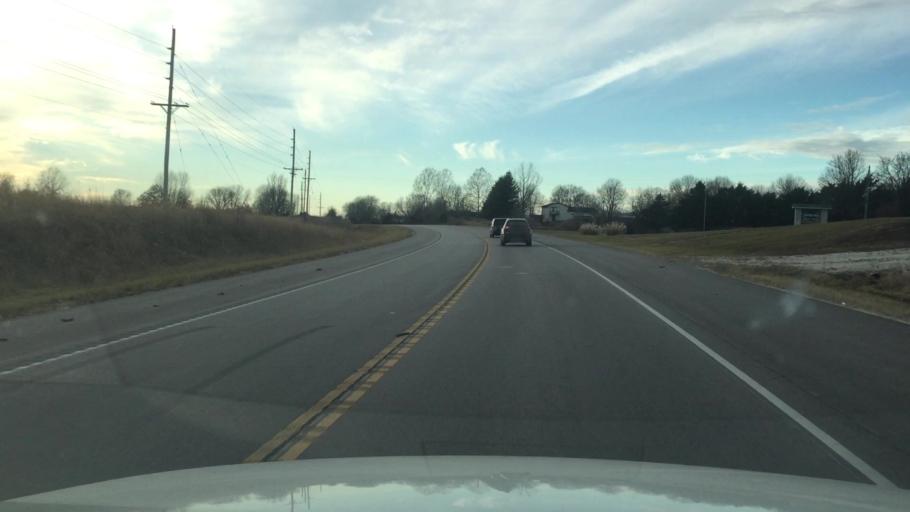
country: US
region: Missouri
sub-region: Miller County
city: Eldon
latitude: 38.3735
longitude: -92.6226
